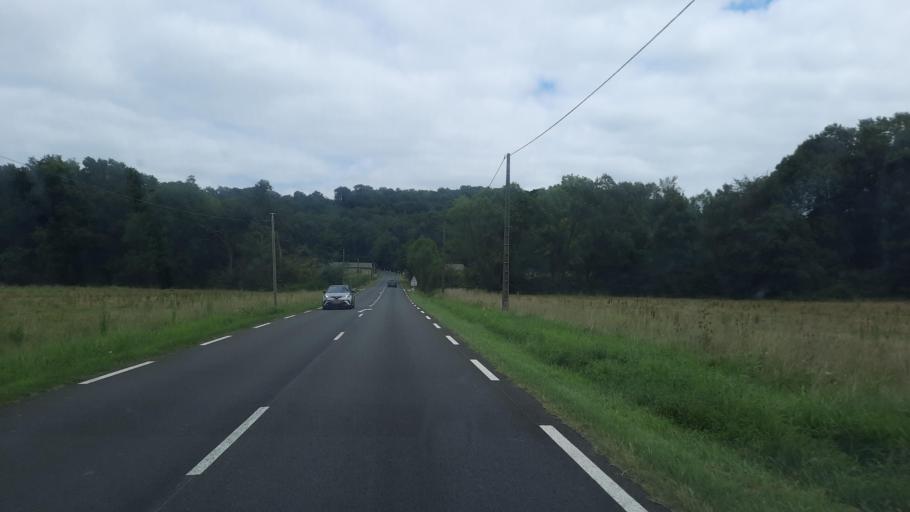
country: FR
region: Midi-Pyrenees
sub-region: Departement des Hautes-Pyrenees
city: Semeac
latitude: 43.2457
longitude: 0.1292
